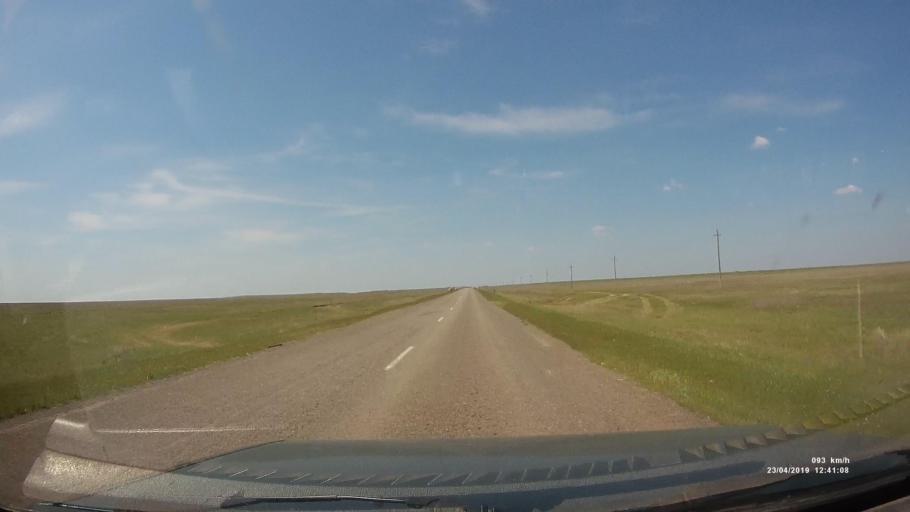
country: RU
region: Kalmykiya
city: Yashalta
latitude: 46.4458
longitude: 42.6857
